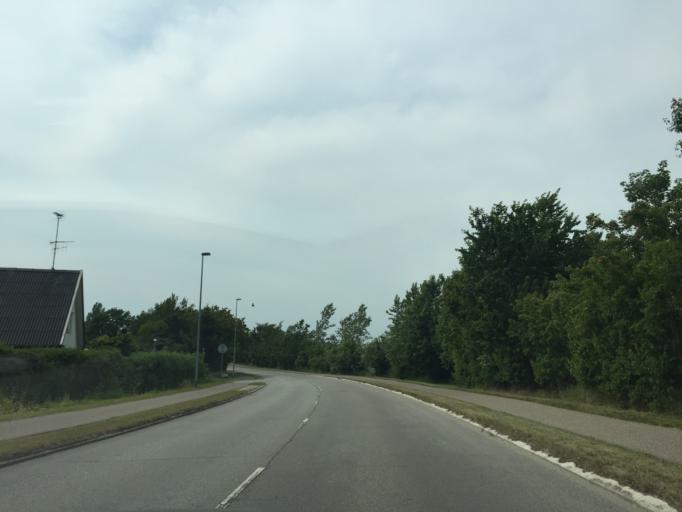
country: DK
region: Capital Region
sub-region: Hoje-Taastrup Kommune
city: Flong
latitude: 55.6532
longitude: 12.1812
